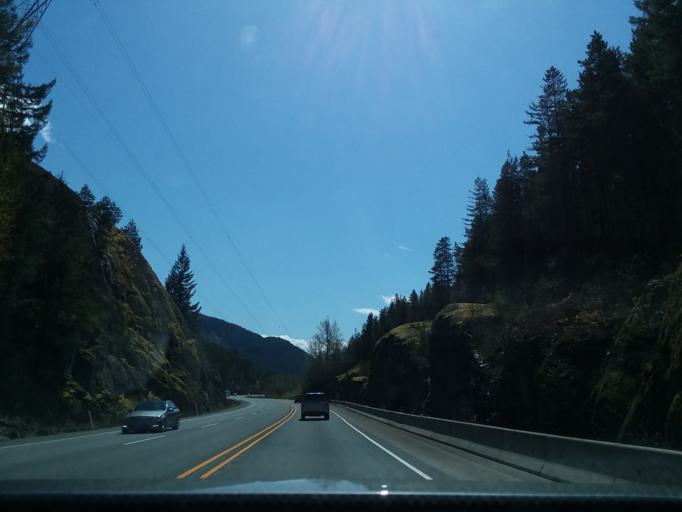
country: CA
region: British Columbia
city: Whistler
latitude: 49.8949
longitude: -123.1618
